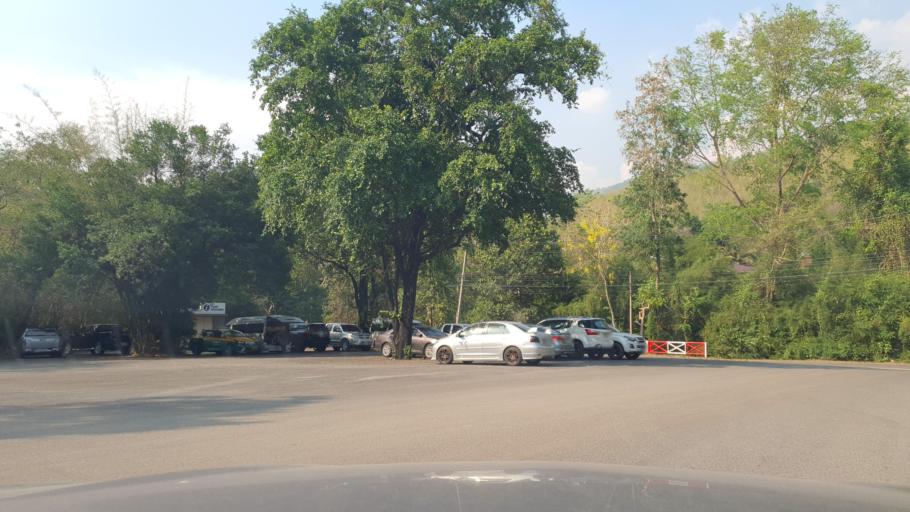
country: TH
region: Kanchanaburi
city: Si Sawat
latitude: 14.3761
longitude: 99.1433
